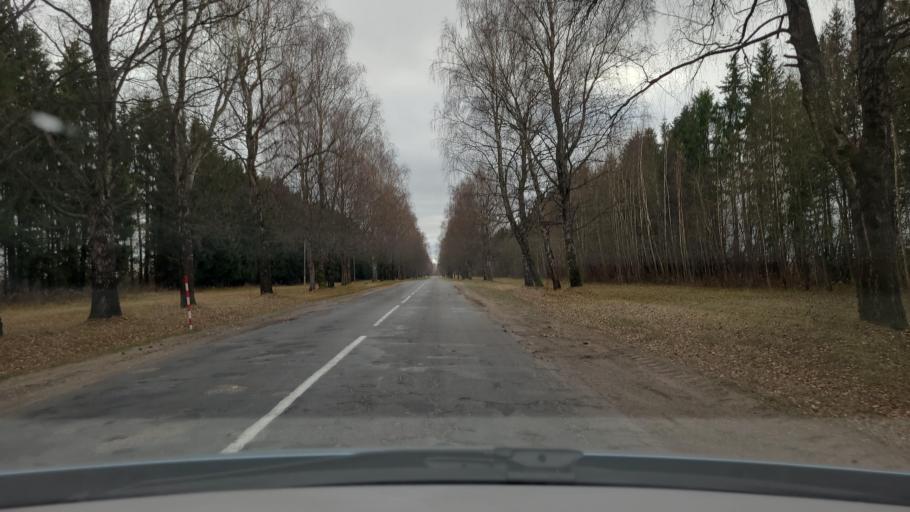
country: BY
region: Minsk
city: Khalopyenichy
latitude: 54.4938
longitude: 28.9549
